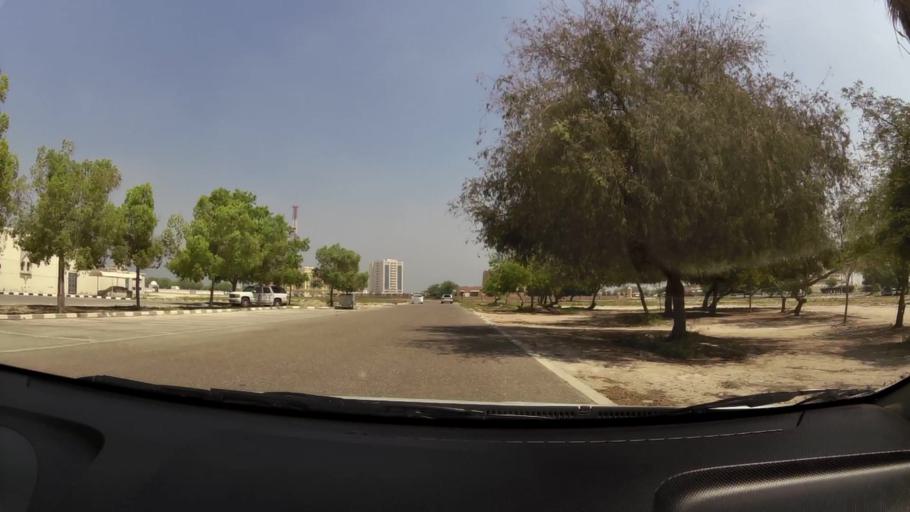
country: AE
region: Umm al Qaywayn
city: Umm al Qaywayn
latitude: 25.5745
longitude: 55.5645
